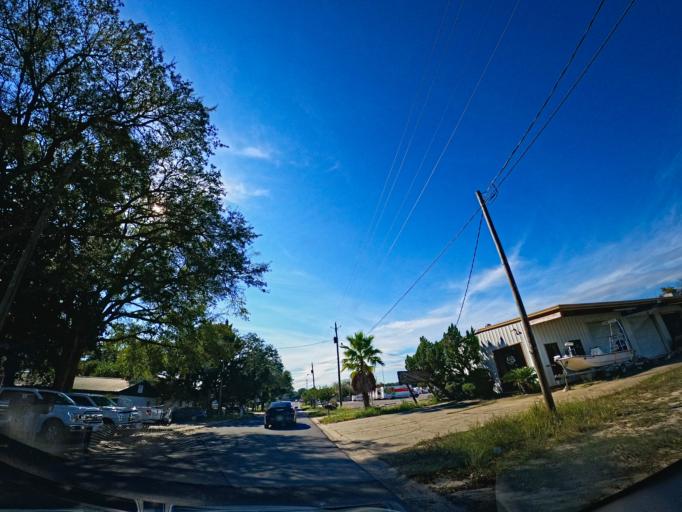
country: US
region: Florida
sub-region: Okaloosa County
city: Fort Walton Beach
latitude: 30.4204
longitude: -86.6110
